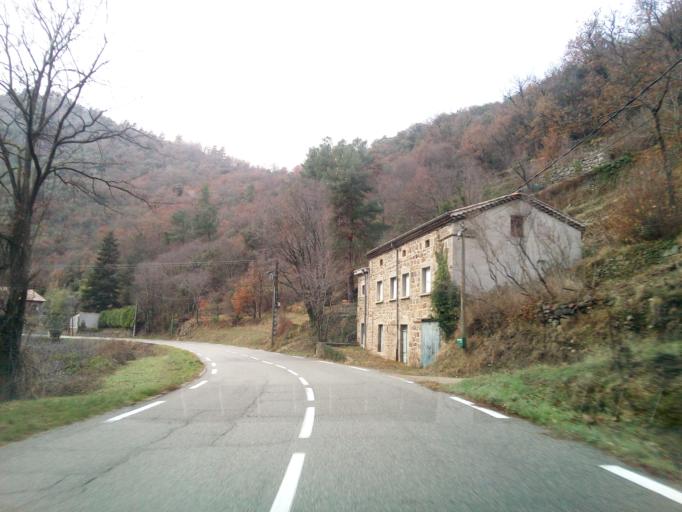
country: FR
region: Rhone-Alpes
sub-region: Departement de l'Ardeche
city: Saint-Sauveur-de-Montagut
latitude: 44.8601
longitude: 4.5616
